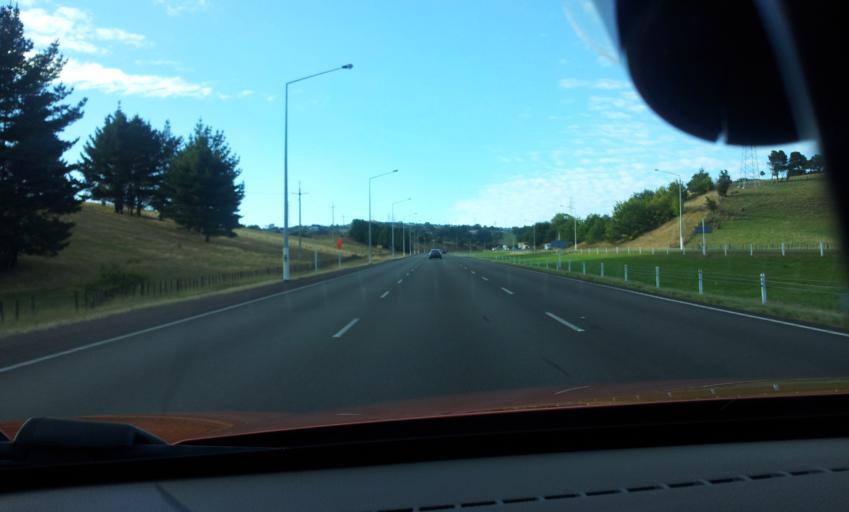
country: NZ
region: Auckland
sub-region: Auckland
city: Pukekohe East
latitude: -37.1612
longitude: 174.9810
